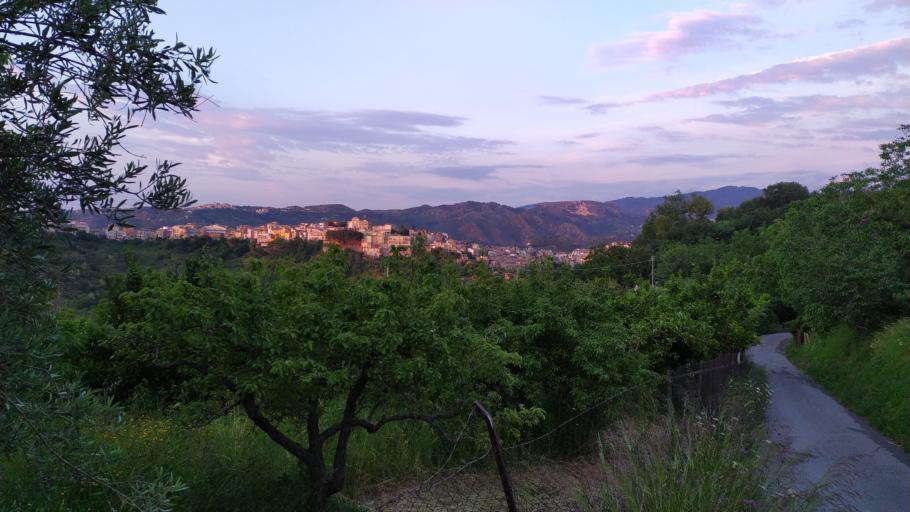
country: IT
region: Sicily
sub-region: Messina
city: San Pier Niceto
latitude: 38.1585
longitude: 15.3395
